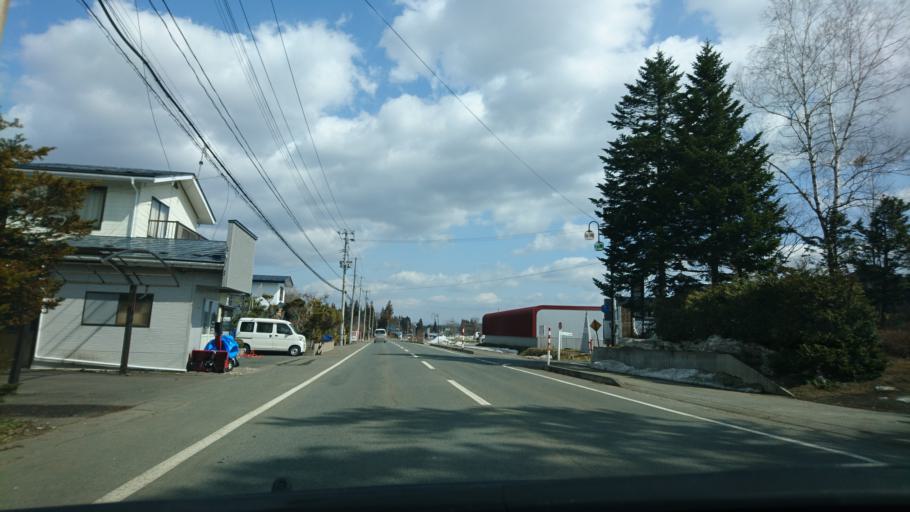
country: JP
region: Iwate
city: Shizukuishi
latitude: 39.6451
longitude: 140.9434
